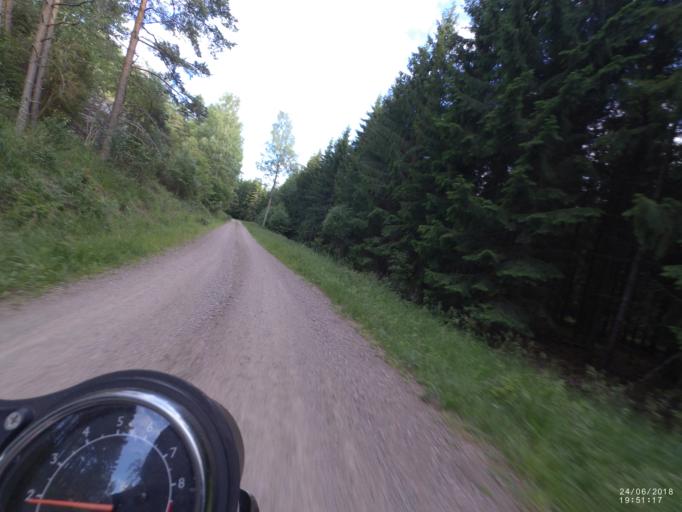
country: SE
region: Soedermanland
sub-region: Oxelosunds Kommun
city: Oxelosund
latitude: 58.7732
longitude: 17.1515
